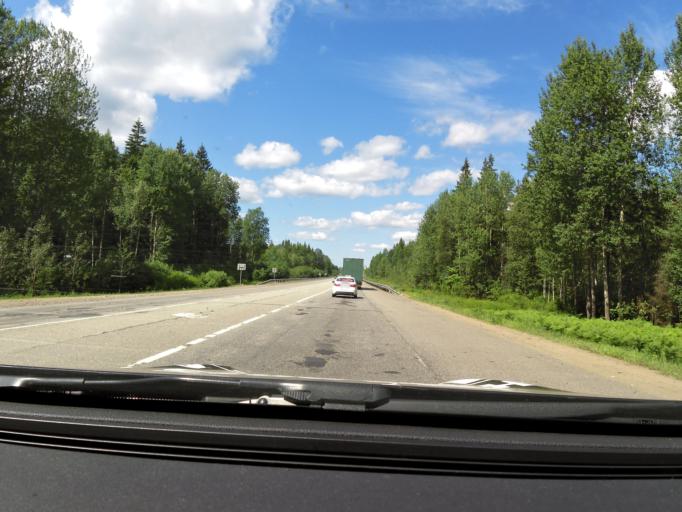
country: RU
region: Tverskaya
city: Kuzhenkino
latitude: 57.7535
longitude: 33.9776
